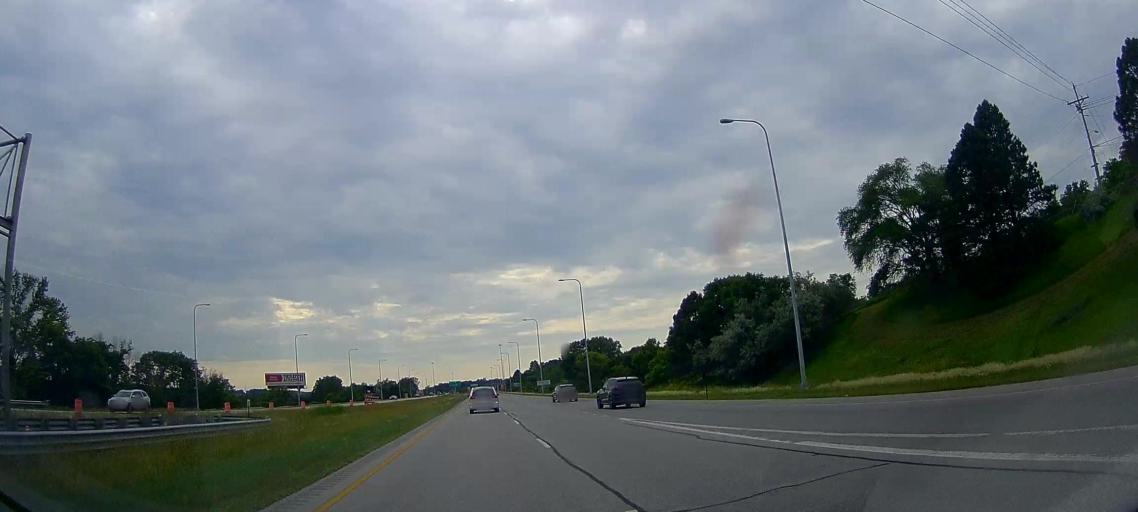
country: US
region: Iowa
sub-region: Pottawattamie County
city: Carter Lake
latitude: 41.3452
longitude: -95.9700
